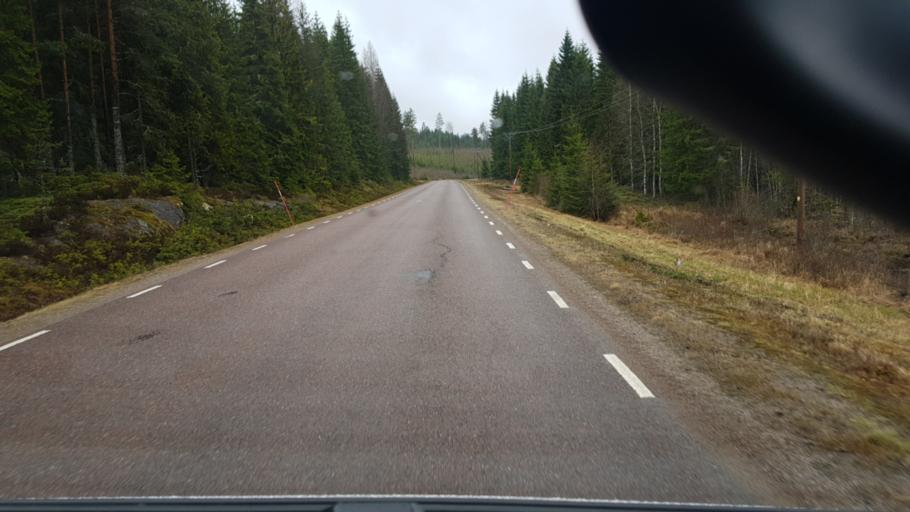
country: SE
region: Vaermland
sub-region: Eda Kommun
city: Charlottenberg
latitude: 59.9409
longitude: 12.3832
